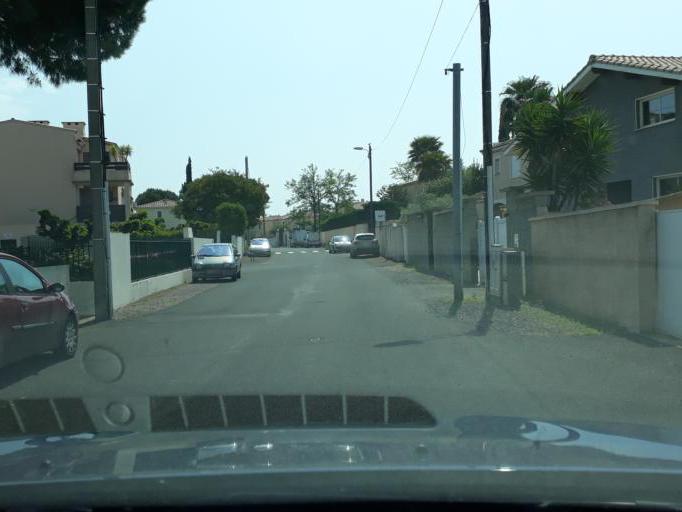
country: FR
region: Languedoc-Roussillon
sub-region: Departement de l'Herault
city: Agde
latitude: 43.2846
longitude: 3.4562
